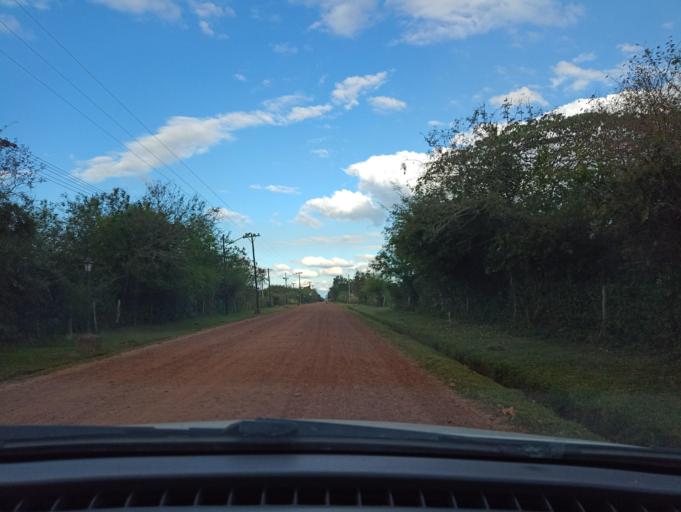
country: AR
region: Corrientes
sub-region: Departamento de San Miguel
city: San Miguel
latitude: -28.5385
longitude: -57.1736
